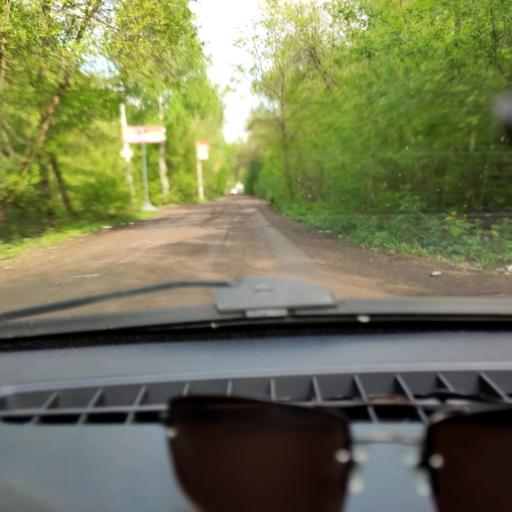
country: RU
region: Bashkortostan
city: Ufa
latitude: 54.6986
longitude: 55.9342
